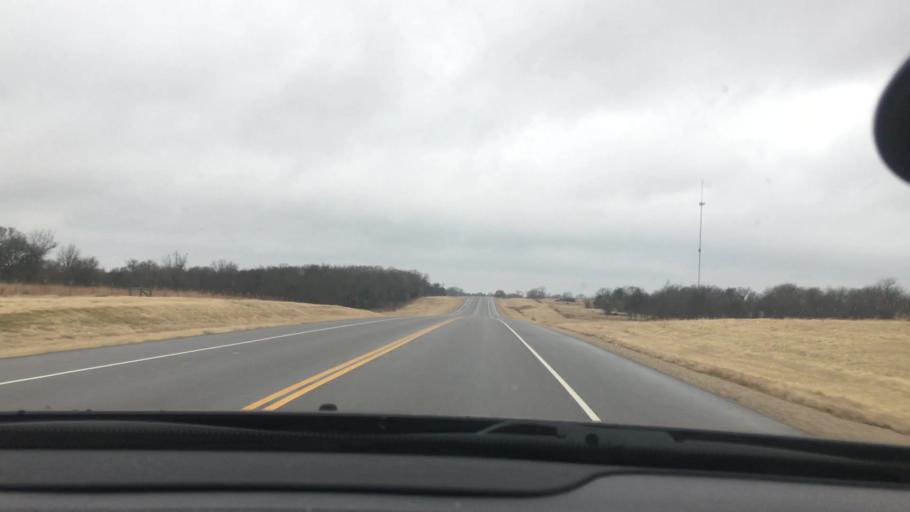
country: US
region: Oklahoma
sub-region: Johnston County
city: Tishomingo
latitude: 34.3250
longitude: -96.6635
